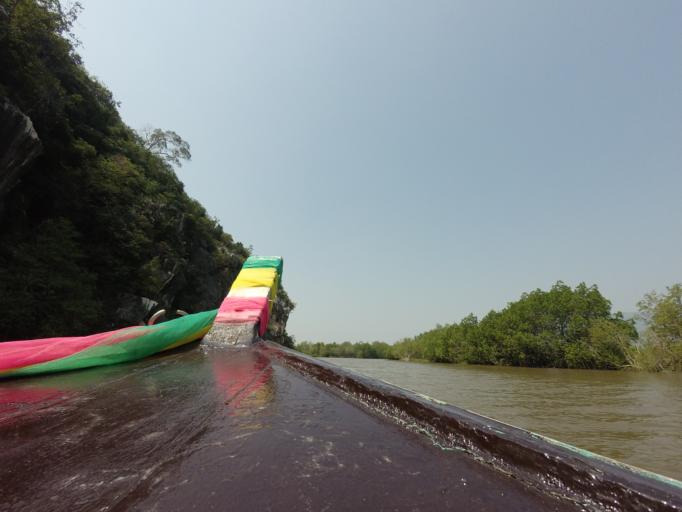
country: TH
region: Prachuap Khiri Khan
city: Kui Buri
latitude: 12.1419
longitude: 99.9542
